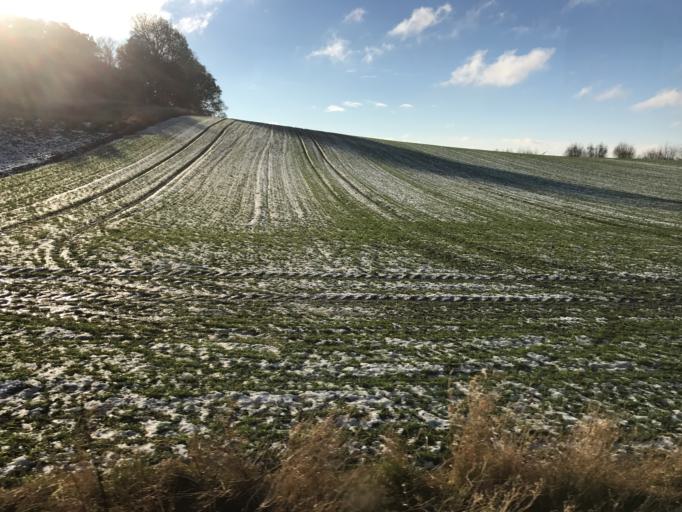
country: DK
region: Zealand
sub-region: Stevns Kommune
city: Harlev
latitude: 55.3498
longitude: 12.3145
